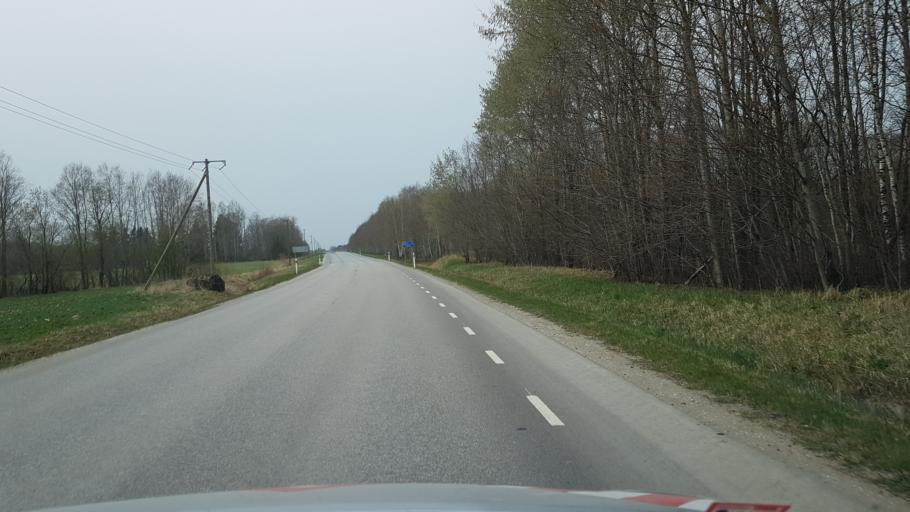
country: EE
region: Harju
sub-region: Joelaehtme vald
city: Loo
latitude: 59.3885
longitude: 24.9883
